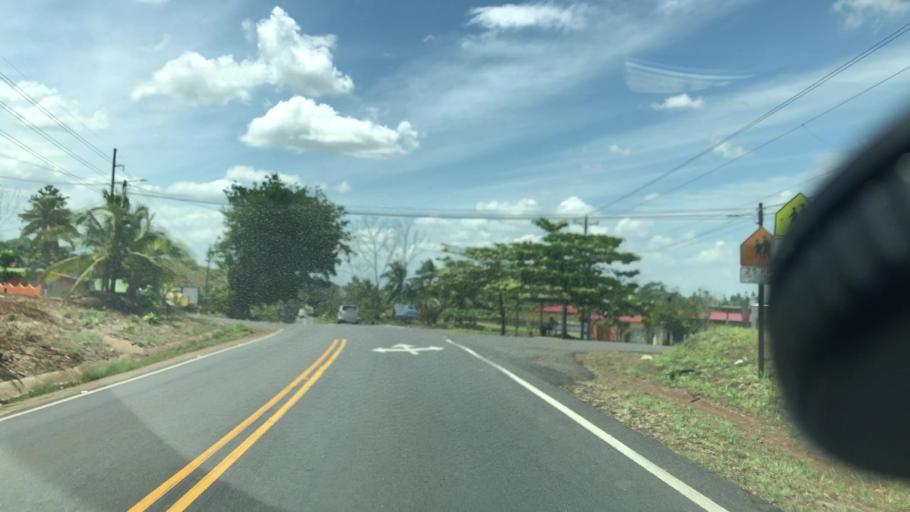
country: CR
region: Alajuela
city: Pital
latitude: 10.4586
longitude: -84.3912
